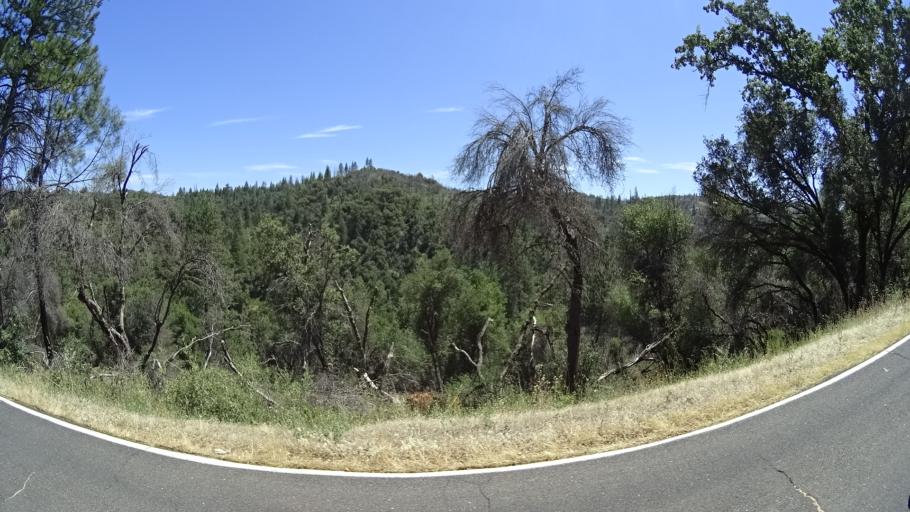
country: US
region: California
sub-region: Calaveras County
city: Mountain Ranch
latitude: 38.2174
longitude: -120.4751
